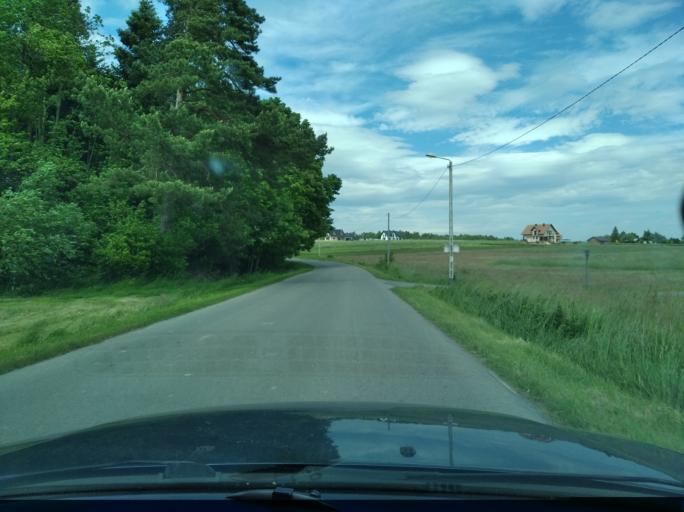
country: PL
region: Subcarpathian Voivodeship
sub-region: Powiat ropczycko-sedziszowski
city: Ropczyce
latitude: 50.0040
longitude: 21.6142
